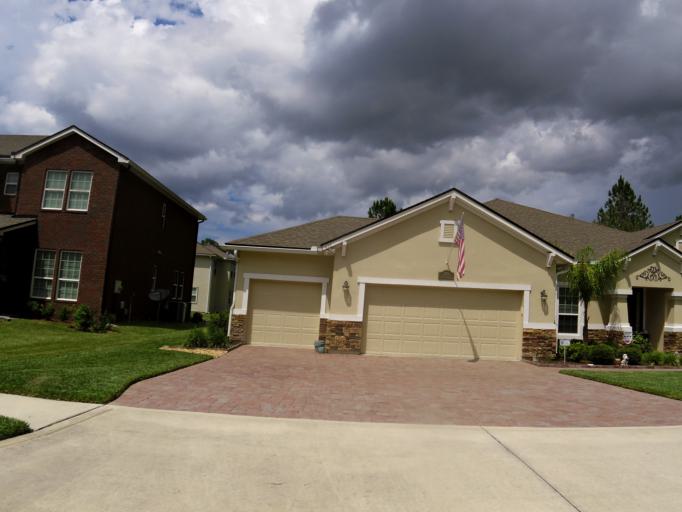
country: US
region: Florida
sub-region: Saint Johns County
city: Fruit Cove
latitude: 30.0682
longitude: -81.6419
